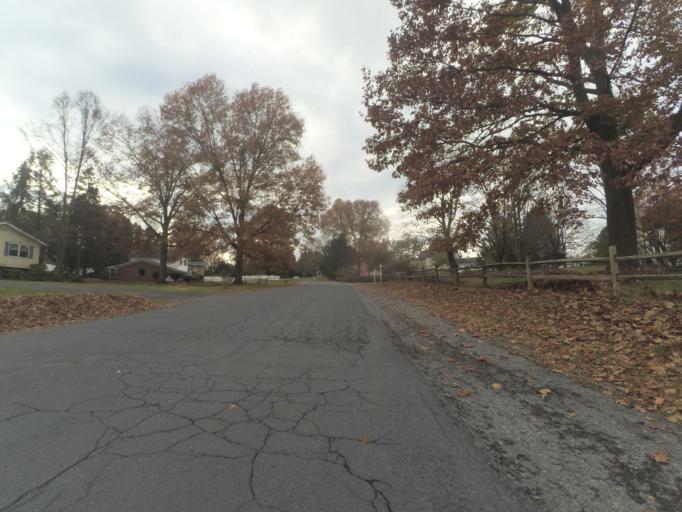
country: US
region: Pennsylvania
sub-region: Centre County
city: Boalsburg
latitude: 40.7780
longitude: -77.8136
